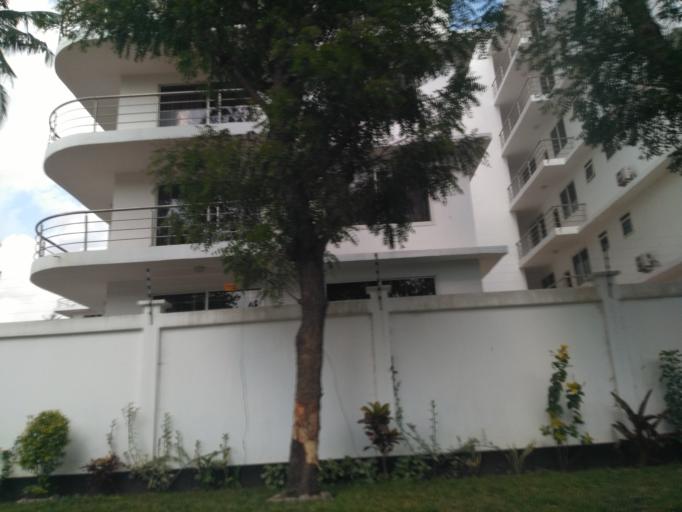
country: TZ
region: Dar es Salaam
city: Magomeni
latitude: -6.7407
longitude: 39.2392
